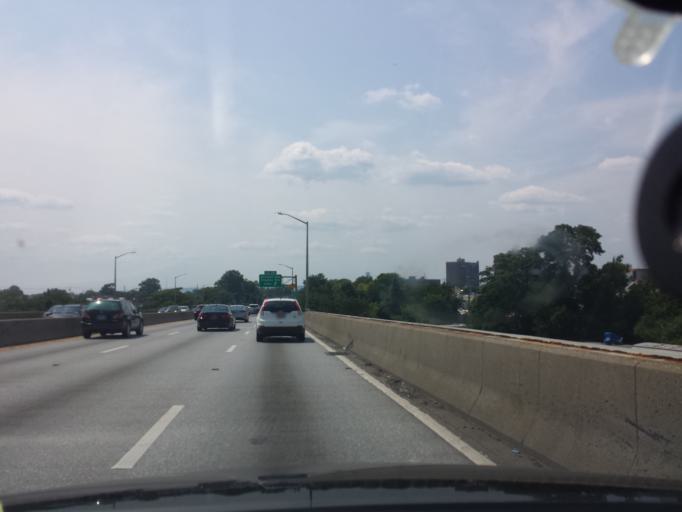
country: US
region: New York
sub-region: Kings County
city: Coney Island
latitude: 40.5832
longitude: -73.9817
